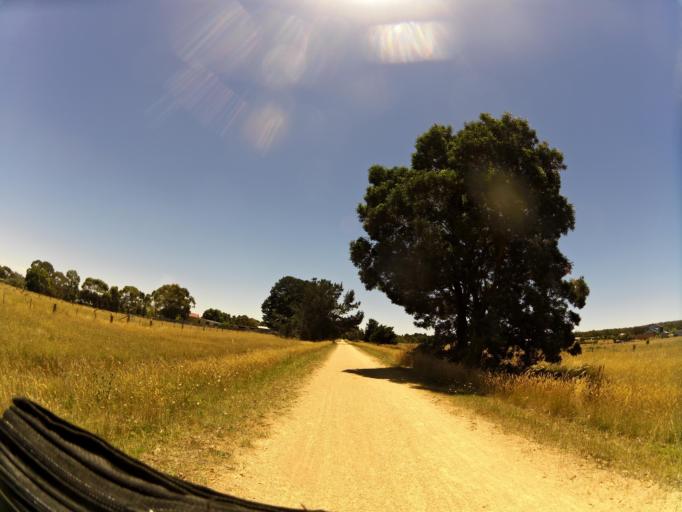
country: AU
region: Victoria
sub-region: Ballarat North
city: Delacombe
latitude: -37.5982
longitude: 143.7188
